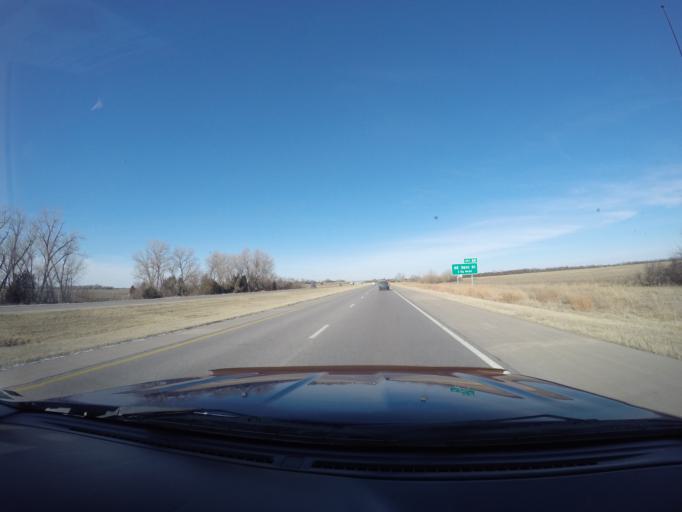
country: US
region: Kansas
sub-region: Harvey County
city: Newton
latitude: 37.9775
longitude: -97.3268
